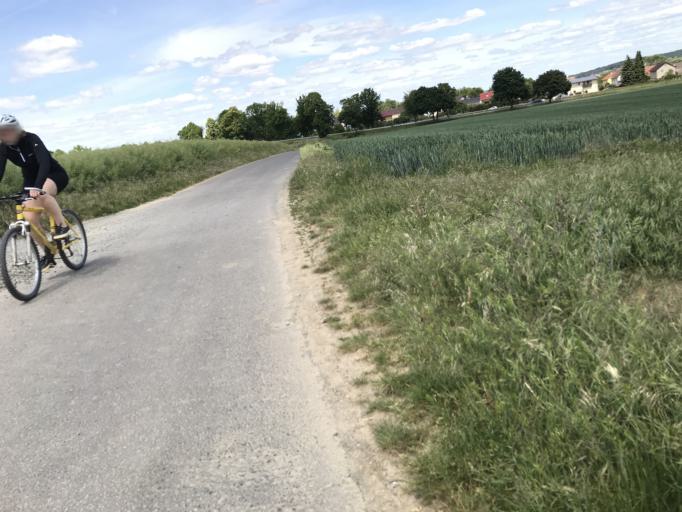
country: DE
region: Hesse
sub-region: Regierungsbezirk Darmstadt
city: Butzbach
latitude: 50.4516
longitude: 8.6518
